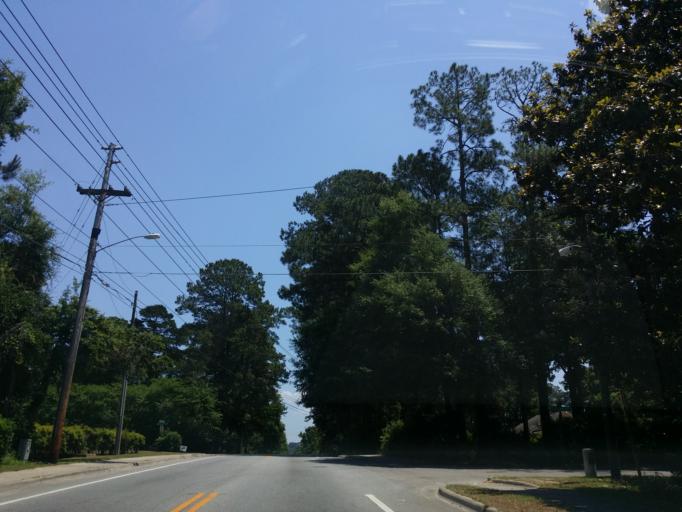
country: US
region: Florida
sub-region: Leon County
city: Tallahassee
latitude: 30.4737
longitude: -84.3409
